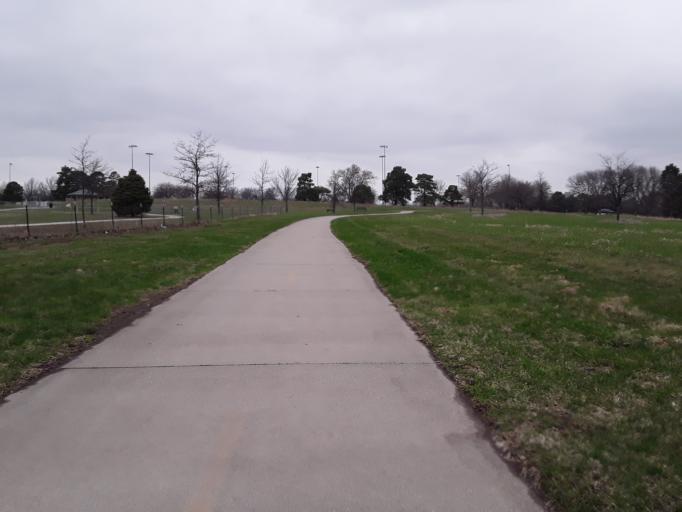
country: US
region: Nebraska
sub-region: Lancaster County
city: Lincoln
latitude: 40.8483
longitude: -96.6074
